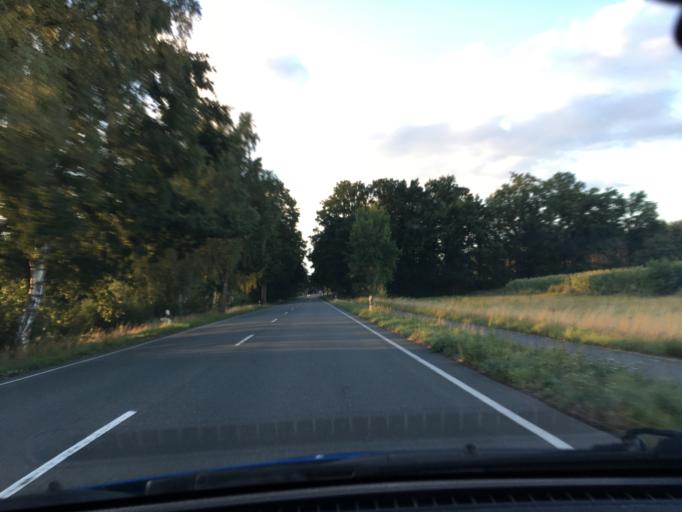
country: DE
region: Lower Saxony
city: Bergen
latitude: 52.7408
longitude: 9.9774
